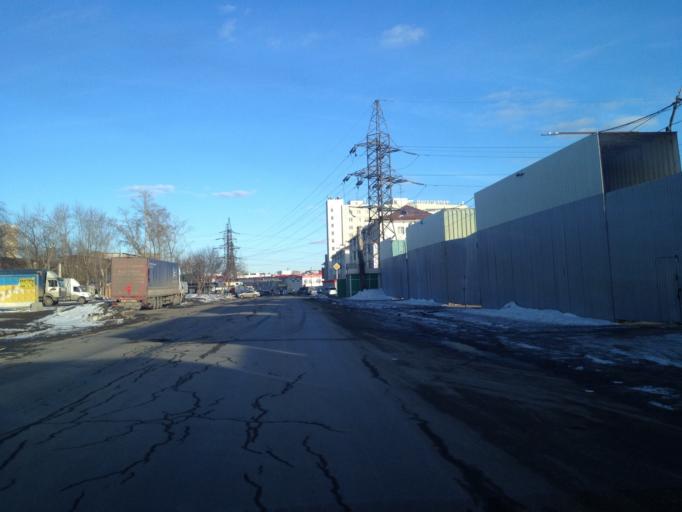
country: RU
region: Sverdlovsk
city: Shuvakish
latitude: 56.8628
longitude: 60.5334
